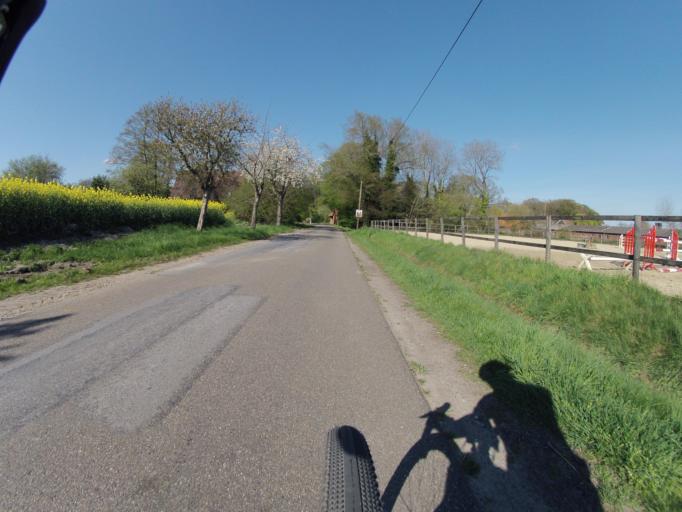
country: DE
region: Lower Saxony
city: Isterberg
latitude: 52.3441
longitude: 7.1384
